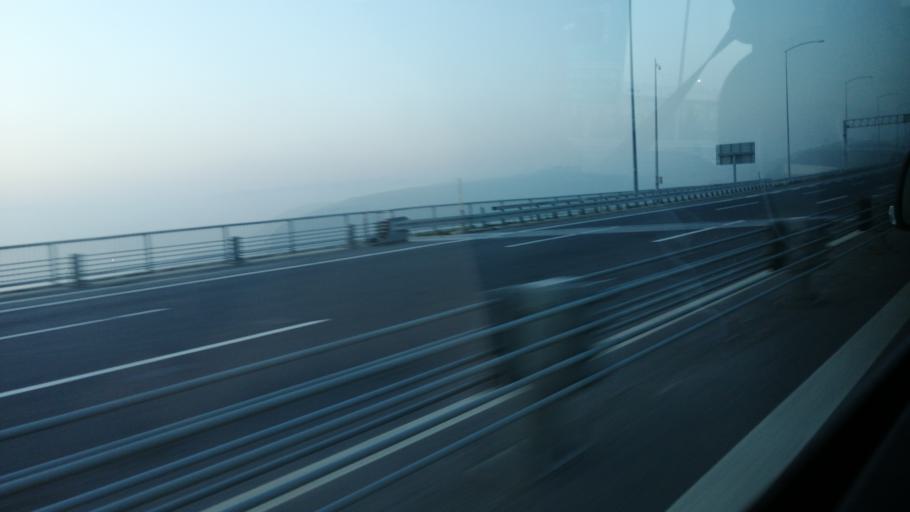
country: TR
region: Kocaeli
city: Tavsanli
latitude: 40.7699
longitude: 29.5183
